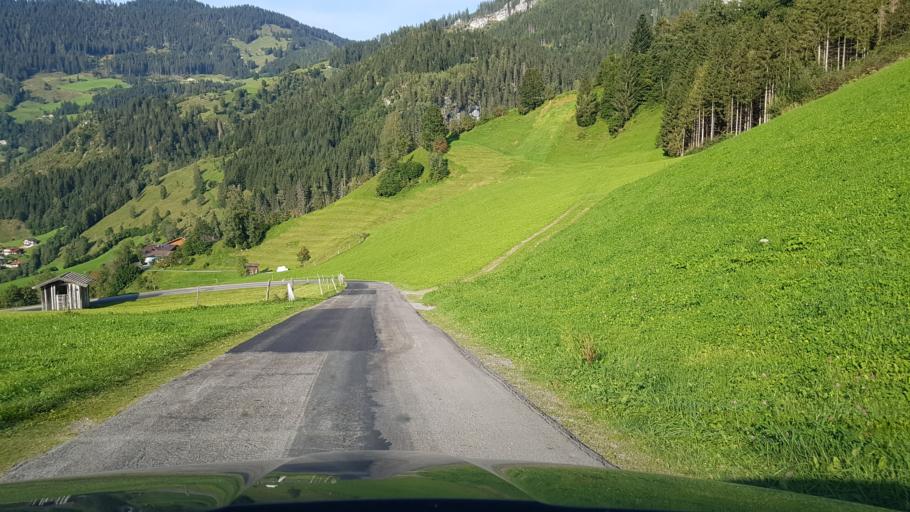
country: AT
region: Salzburg
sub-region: Politischer Bezirk Sankt Johann im Pongau
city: Sankt Johann im Pongau
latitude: 47.2750
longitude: 13.2181
